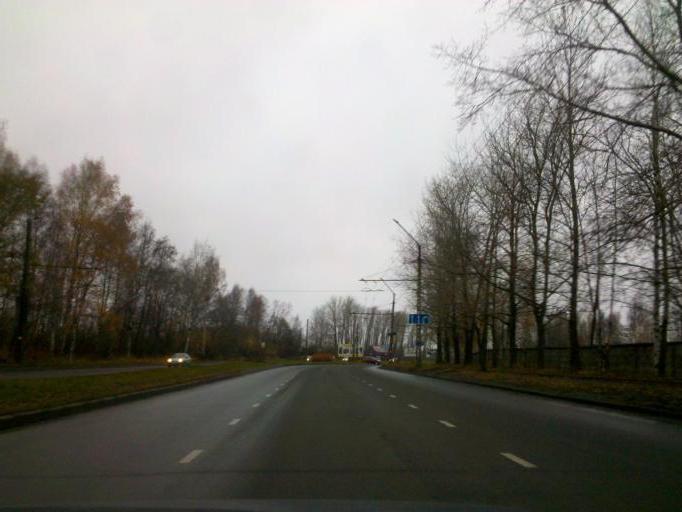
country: RU
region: Republic of Karelia
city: Petrozavodsk
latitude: 61.8061
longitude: 34.2940
